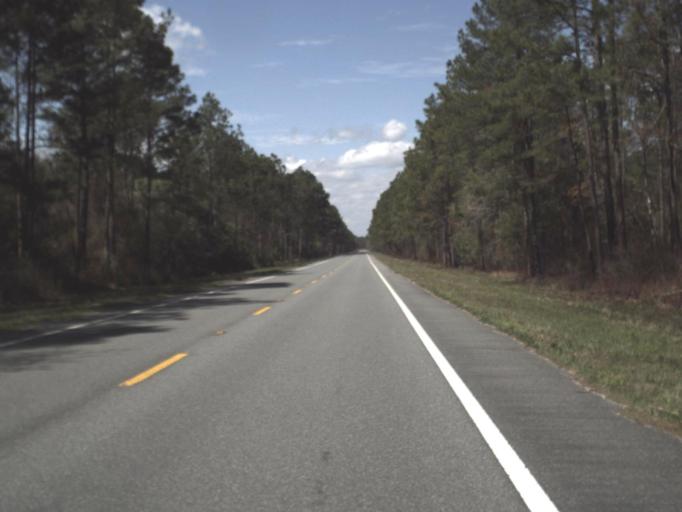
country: US
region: Florida
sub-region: Gadsden County
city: Midway
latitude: 30.3766
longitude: -84.5577
